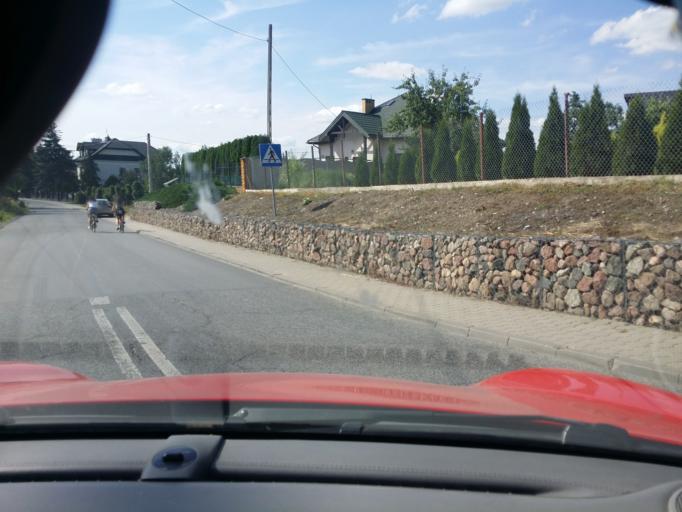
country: PL
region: Masovian Voivodeship
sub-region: Powiat radomski
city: Trablice
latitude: 51.3509
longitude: 21.1374
